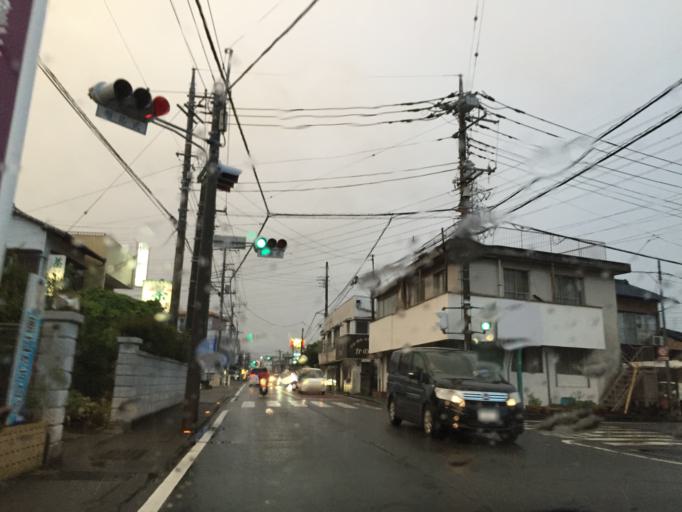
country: JP
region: Shizuoka
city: Mishima
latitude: 35.1405
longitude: 138.9124
